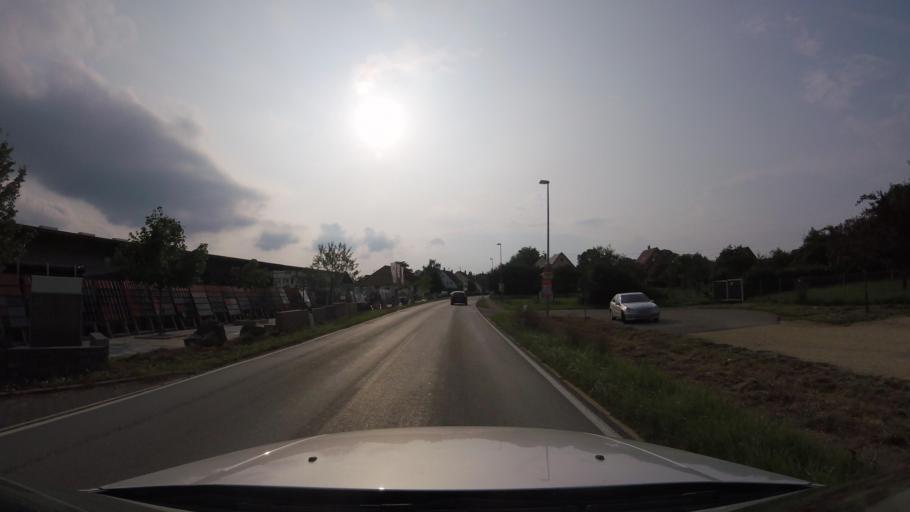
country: DE
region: Baden-Wuerttemberg
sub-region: Regierungsbezirk Stuttgart
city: Alfdorf
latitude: 48.8416
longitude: 9.7285
